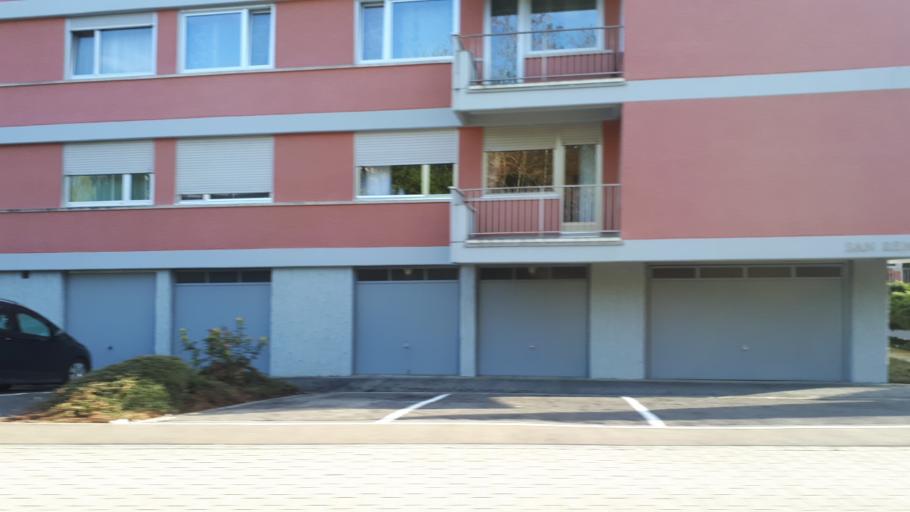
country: LU
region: Luxembourg
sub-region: Canton de Luxembourg
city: Strassen
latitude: 49.6161
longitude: 6.0898
